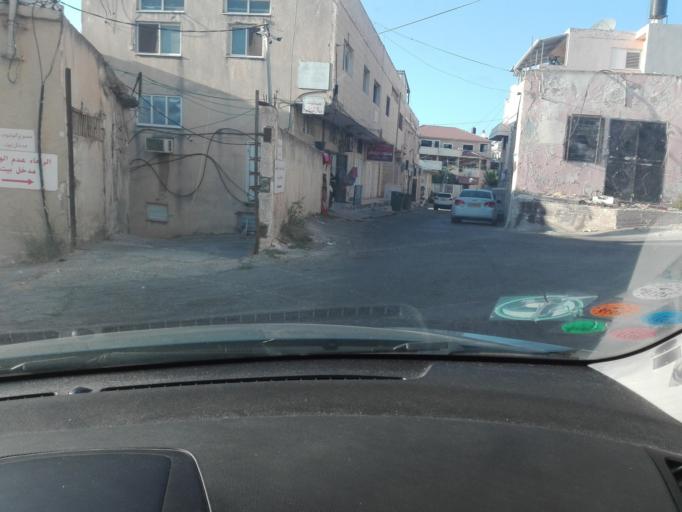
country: PS
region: West Bank
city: Nazlat `Isa
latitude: 32.4145
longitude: 35.0466
